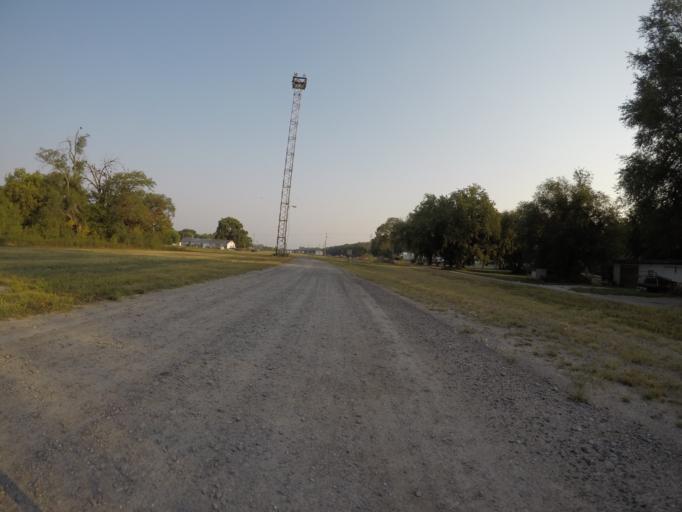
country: US
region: Kansas
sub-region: Marshall County
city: Marysville
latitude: 39.8456
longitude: -96.6494
